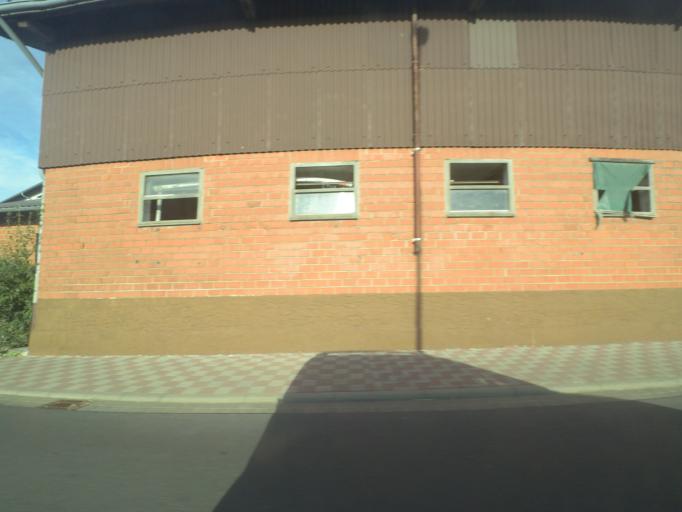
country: DE
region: Hesse
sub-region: Regierungsbezirk Giessen
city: Freiensteinau
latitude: 50.3513
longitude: 9.3977
